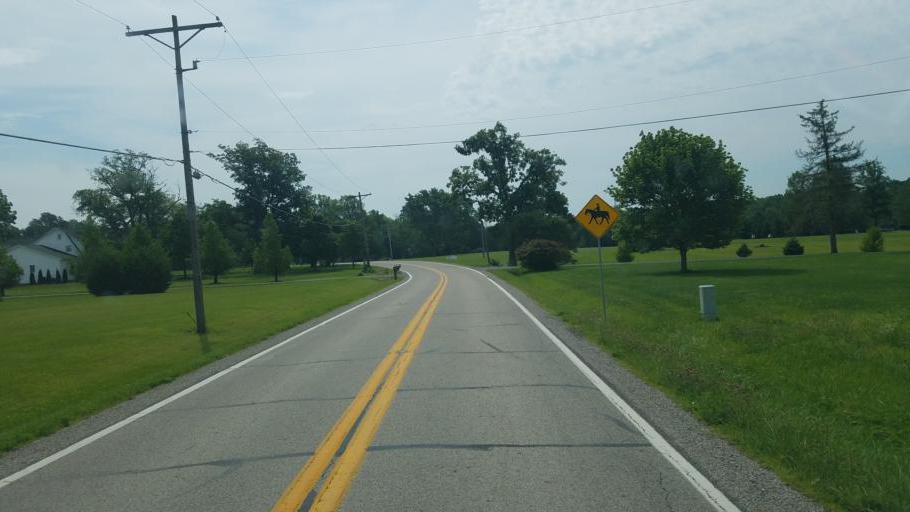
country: US
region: Ohio
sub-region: Madison County
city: West Jefferson
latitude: 39.9167
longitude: -83.2426
